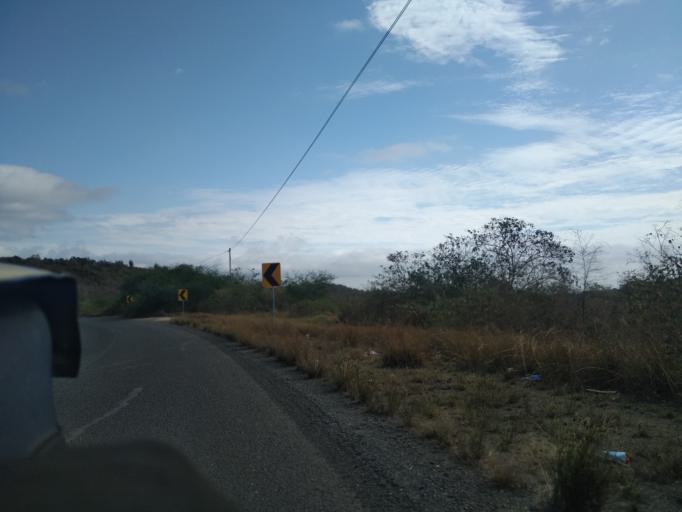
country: EC
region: Manabi
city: Jipijapa
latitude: -1.4435
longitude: -80.7554
